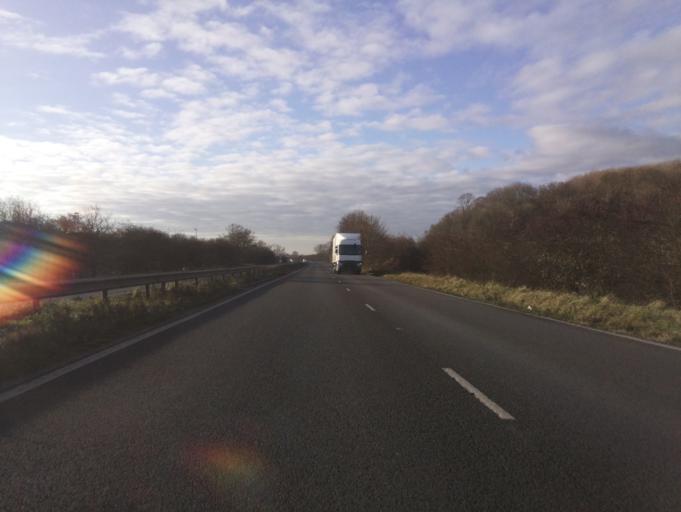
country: GB
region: England
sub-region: Staffordshire
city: Burton upon Trent
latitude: 52.8062
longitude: -1.6653
